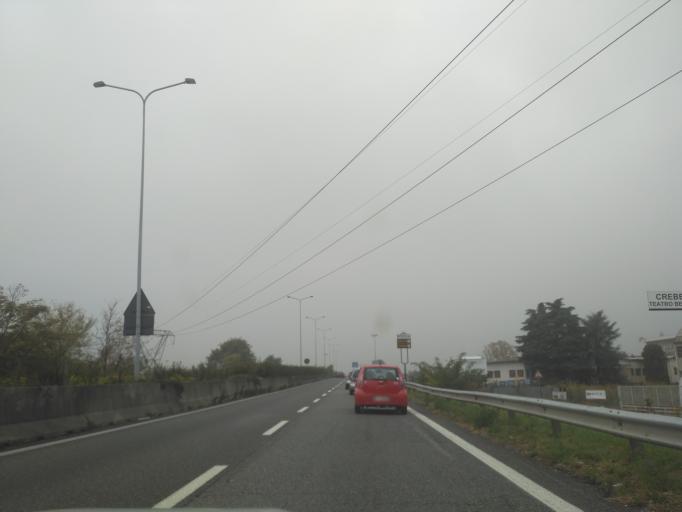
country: IT
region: Lombardy
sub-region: Provincia di Bergamo
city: Orio al Serio
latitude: 45.6754
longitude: 9.6753
